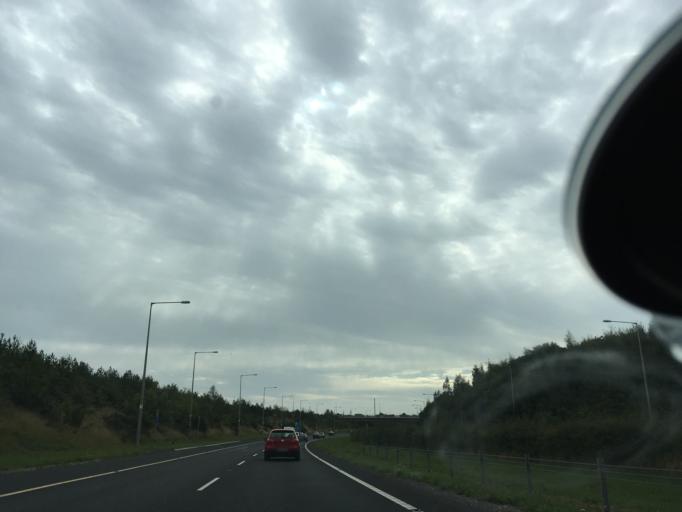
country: IE
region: Leinster
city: Loughlinstown
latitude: 53.2349
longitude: -6.1366
